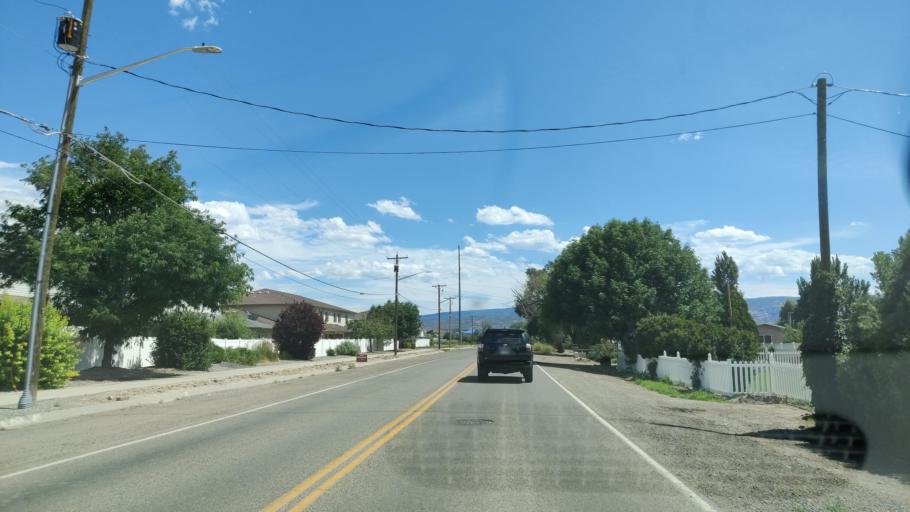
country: US
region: Colorado
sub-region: Mesa County
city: Redlands
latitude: 39.1011
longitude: -108.5988
